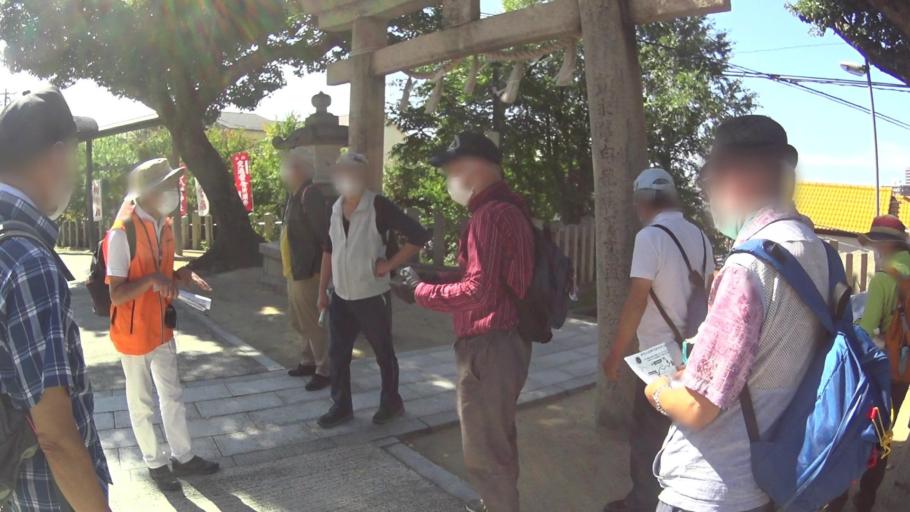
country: JP
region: Osaka
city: Izumiotsu
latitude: 34.4873
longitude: 135.4033
